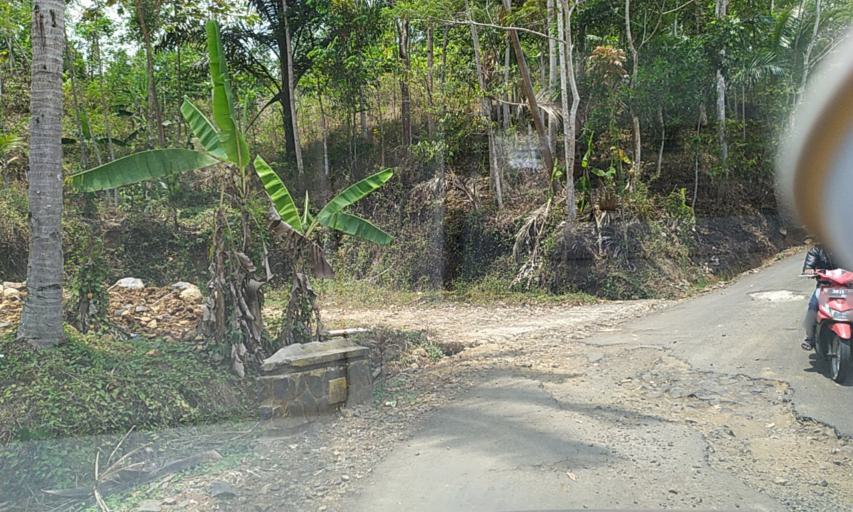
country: ID
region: Central Java
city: Kubang
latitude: -7.2709
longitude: 108.6296
